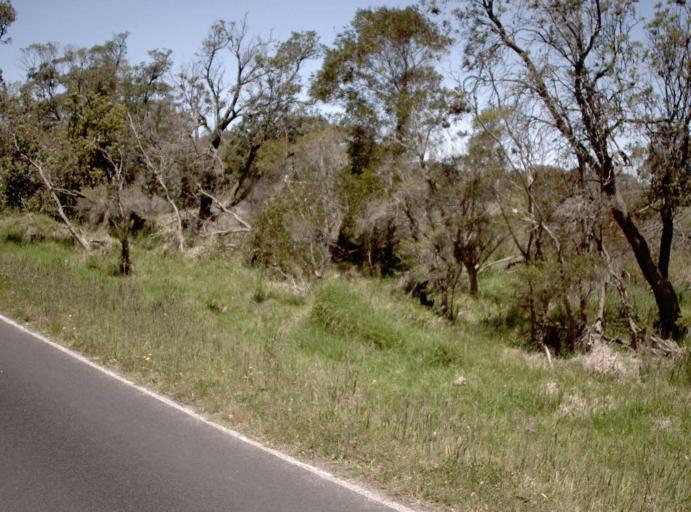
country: AU
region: Victoria
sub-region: Latrobe
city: Morwell
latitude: -38.8544
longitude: 146.2453
